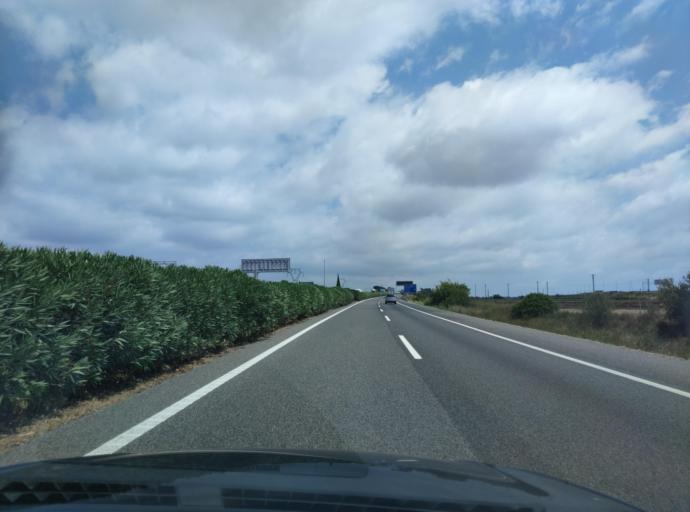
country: ES
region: Catalonia
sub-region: Provincia de Tarragona
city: Amposta
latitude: 40.7484
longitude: 0.5960
